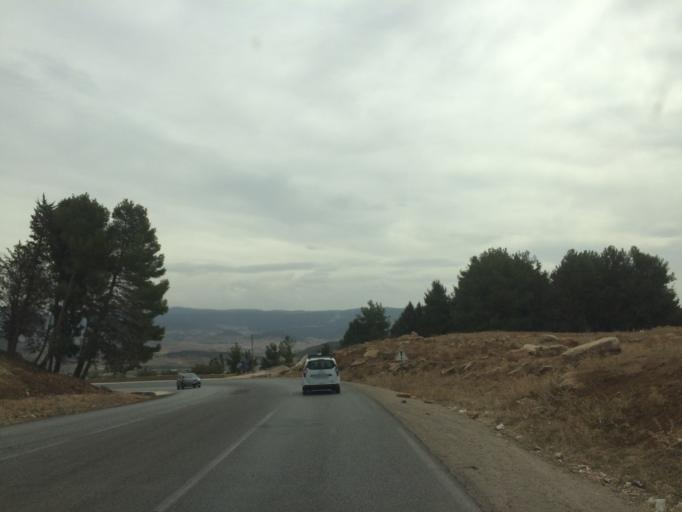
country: MA
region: Meknes-Tafilalet
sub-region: Ifrane
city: Azrou
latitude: 33.4967
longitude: -5.2693
